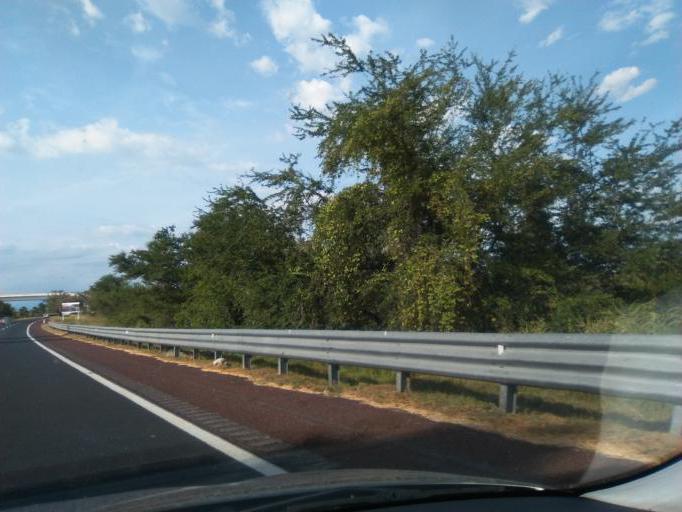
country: MX
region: Morelos
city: Puente de Ixtla
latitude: 18.6359
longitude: -99.2949
